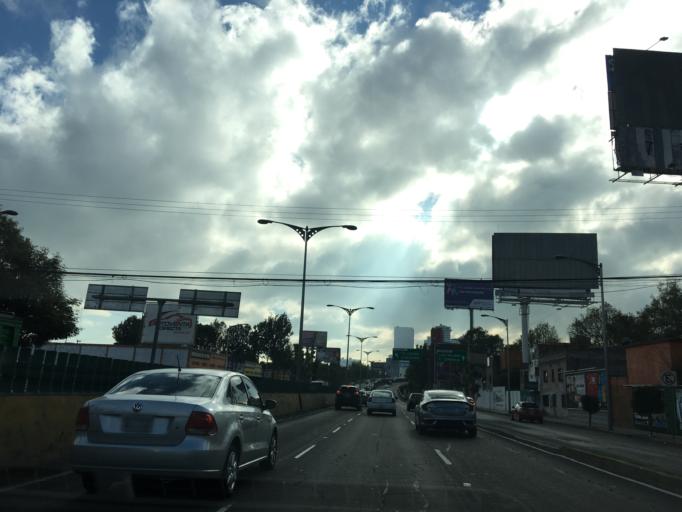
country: MX
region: Mexico City
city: Miguel Hidalgo
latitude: 19.4431
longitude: -99.1955
